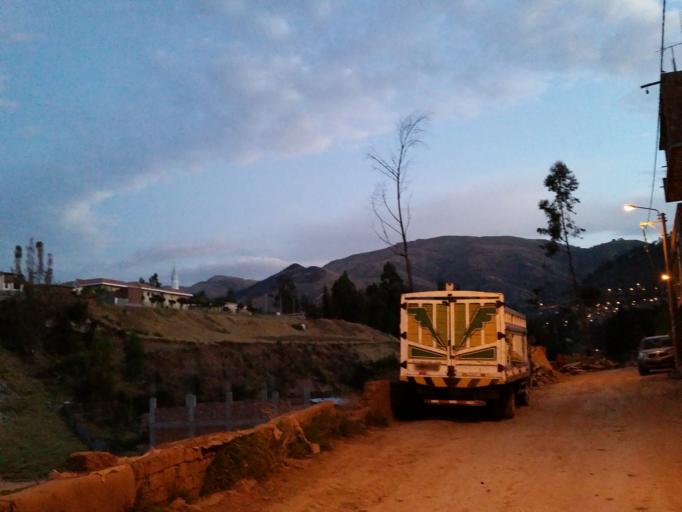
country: PE
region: Cusco
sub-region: Provincia de Cusco
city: Cusco
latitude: -13.5409
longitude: -71.9499
